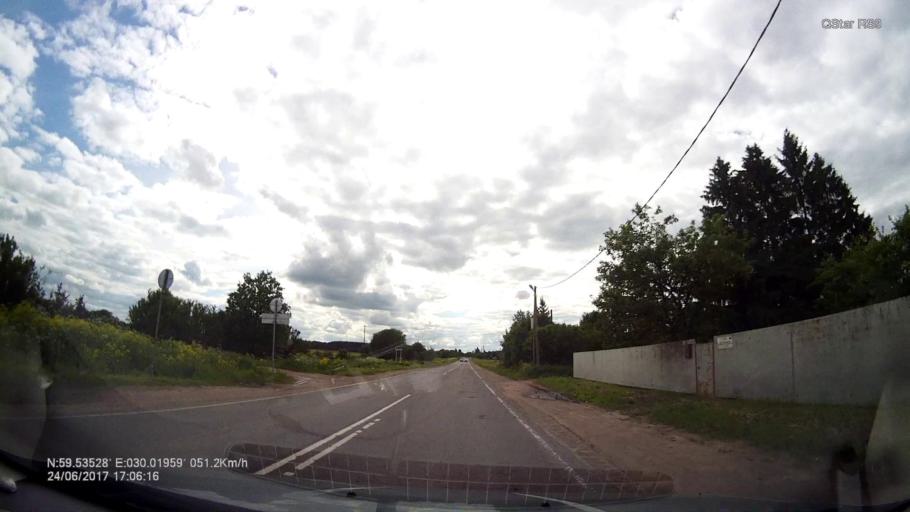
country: RU
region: Leningrad
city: Voyskovitsy
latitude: 59.5353
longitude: 30.0192
